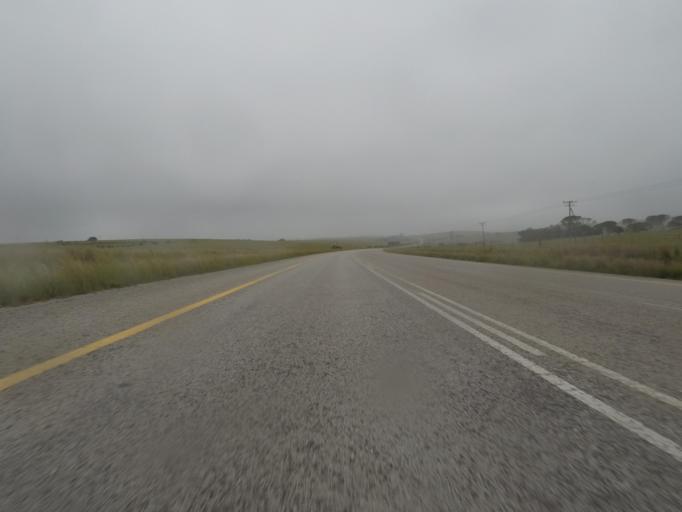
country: ZA
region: Eastern Cape
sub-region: Cacadu District Municipality
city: Grahamstown
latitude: -33.6273
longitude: 26.3086
